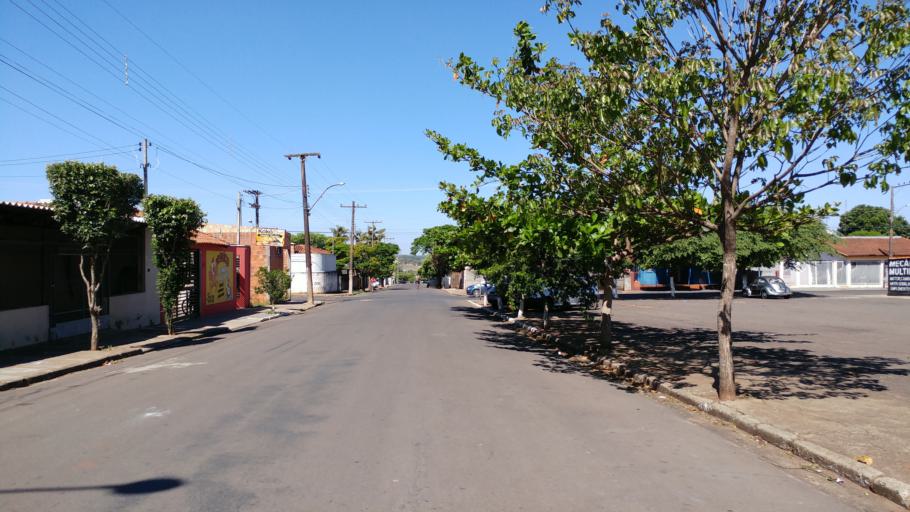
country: BR
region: Sao Paulo
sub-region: Paraguacu Paulista
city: Paraguacu Paulista
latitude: -22.4142
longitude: -50.5716
